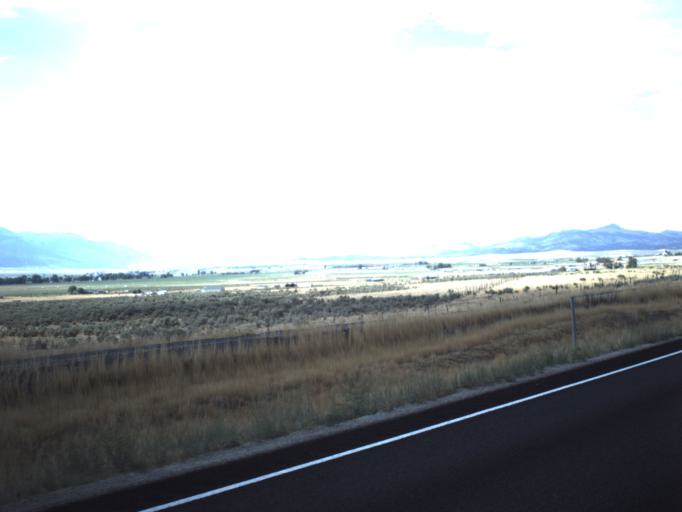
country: US
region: Utah
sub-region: Sanpete County
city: Moroni
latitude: 39.4514
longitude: -111.5434
